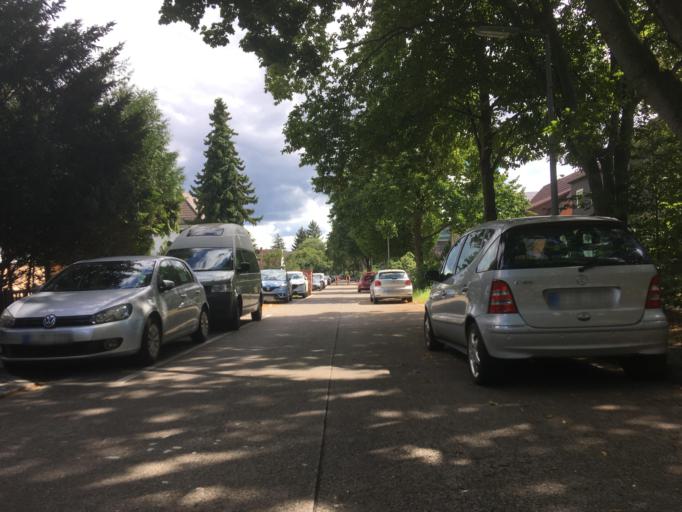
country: DE
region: Berlin
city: Rudow
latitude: 52.4391
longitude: 13.4788
